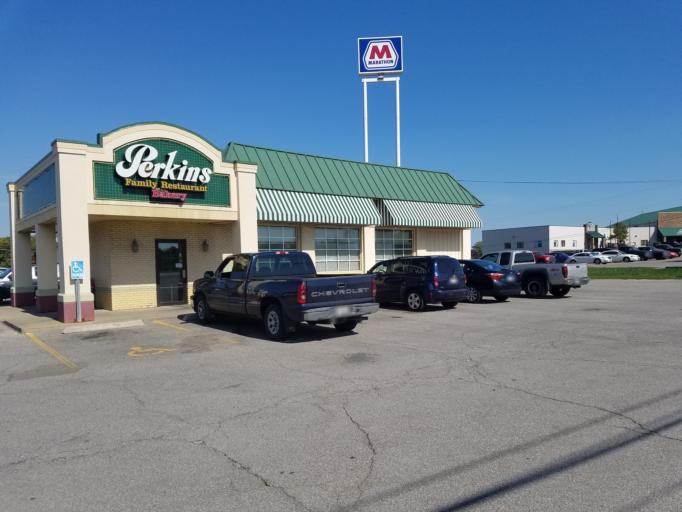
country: US
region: Ohio
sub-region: Ashland County
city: Ashland
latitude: 40.8576
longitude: -82.2515
